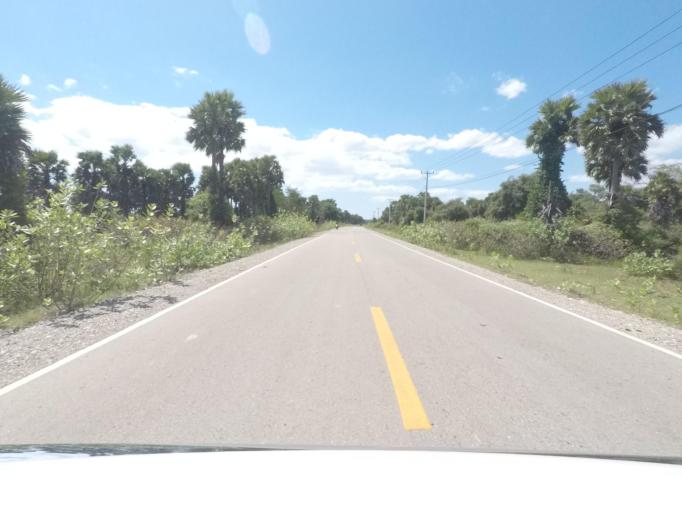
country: TL
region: Lautem
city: Lospalos
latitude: -8.3802
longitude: 126.8639
